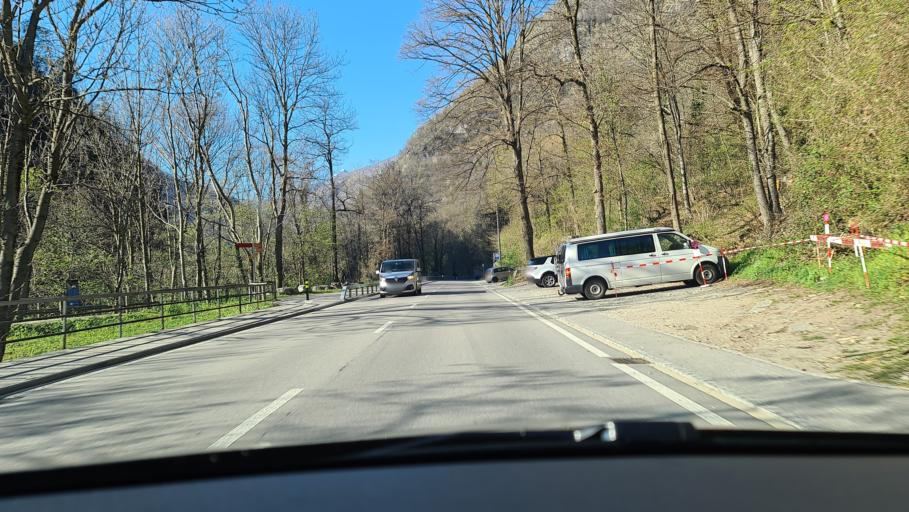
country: CH
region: Ticino
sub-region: Locarno District
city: Losone
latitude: 46.1890
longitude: 8.7568
